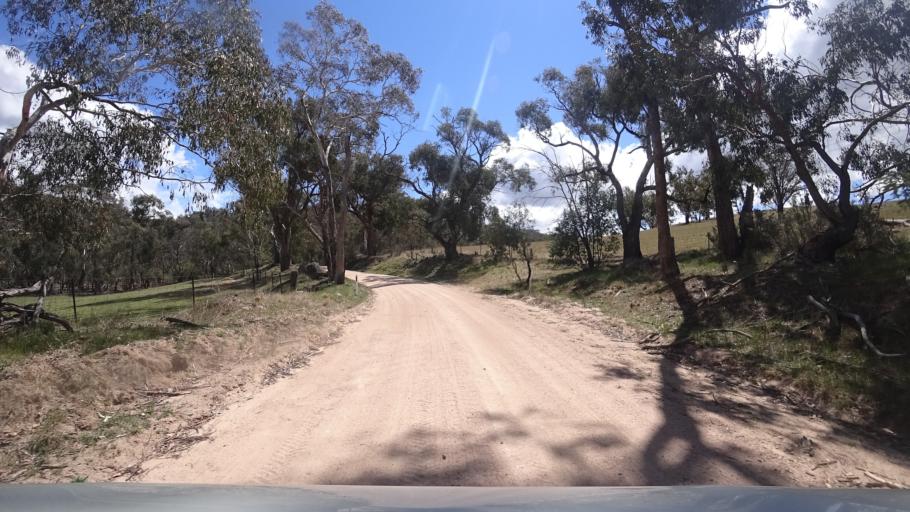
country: AU
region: New South Wales
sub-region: Oberon
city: Oberon
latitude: -33.5521
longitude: 149.9314
